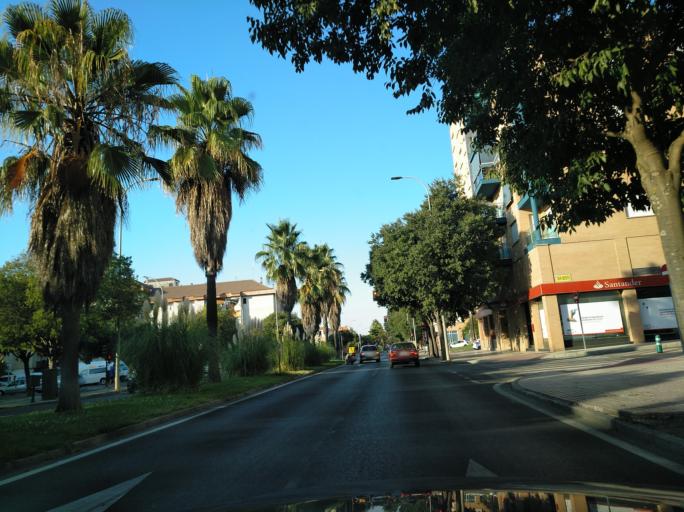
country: ES
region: Extremadura
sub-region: Provincia de Badajoz
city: Badajoz
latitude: 38.8664
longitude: -6.9818
